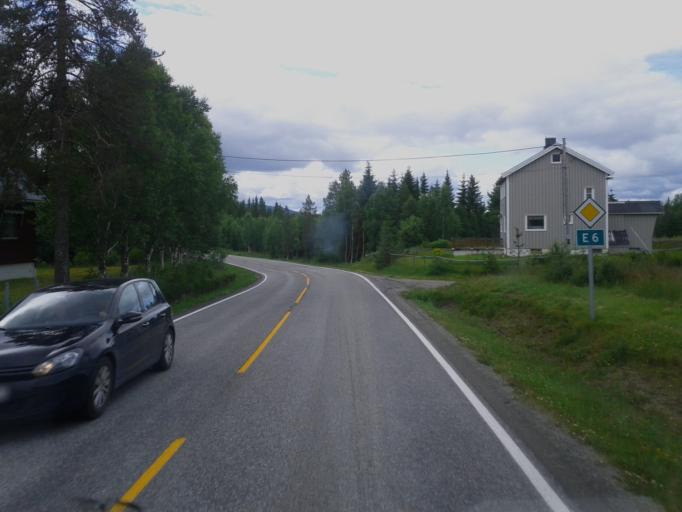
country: NO
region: Nord-Trondelag
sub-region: Hoylandet
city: Hoylandet
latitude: 64.6600
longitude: 12.6492
